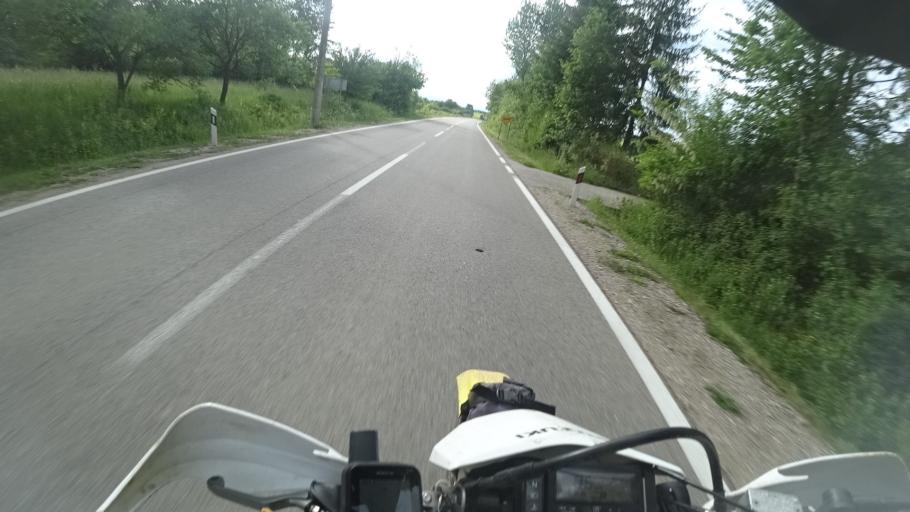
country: HR
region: Licko-Senjska
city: Gospic
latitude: 44.4994
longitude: 15.4545
